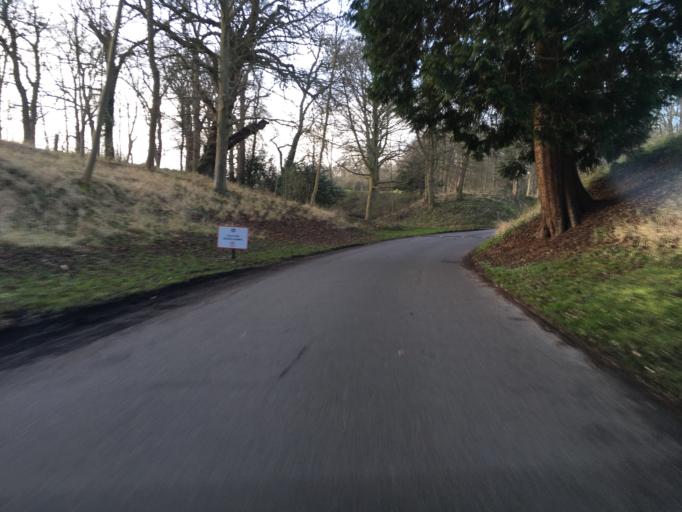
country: GB
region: England
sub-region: Warwickshire
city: Stratford-upon-Avon
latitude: 52.2054
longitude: -1.6939
